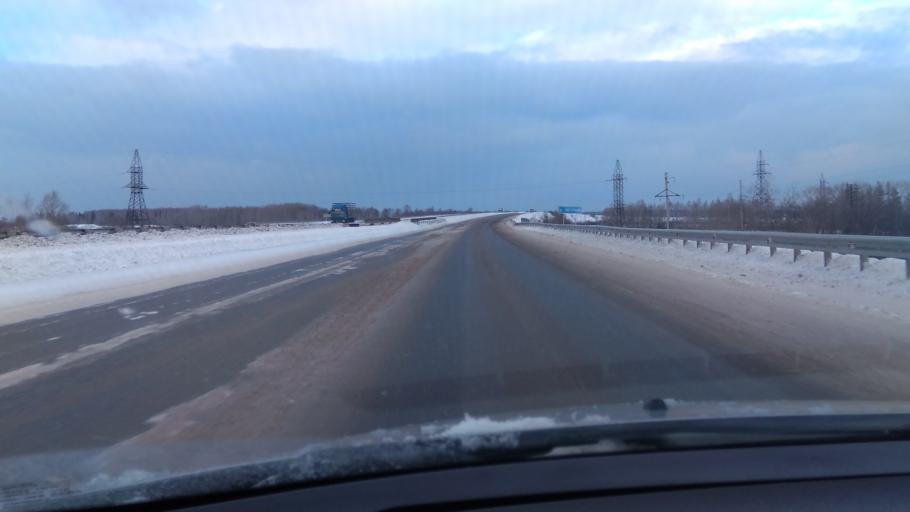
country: RU
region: Sverdlovsk
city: Tsementnyy
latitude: 57.4998
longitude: 60.1740
